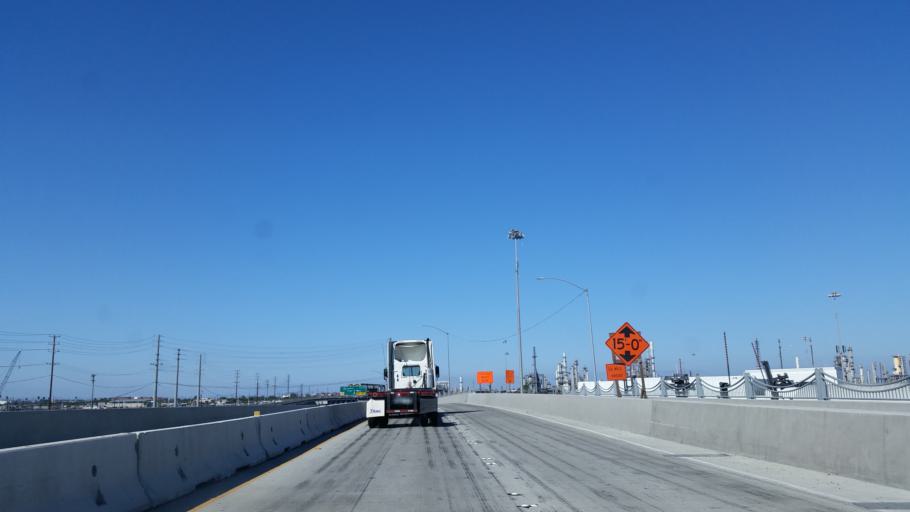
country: US
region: California
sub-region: Los Angeles County
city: Long Beach
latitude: 33.7700
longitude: -118.2400
